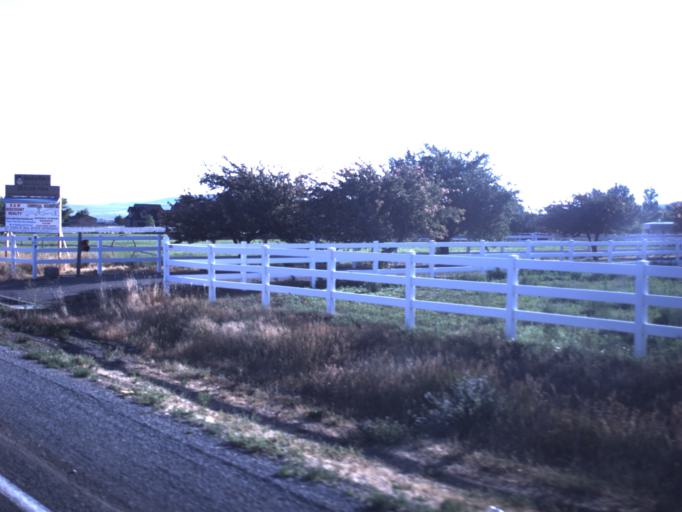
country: US
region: Utah
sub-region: Iron County
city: Enoch
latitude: 37.7347
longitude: -113.0552
